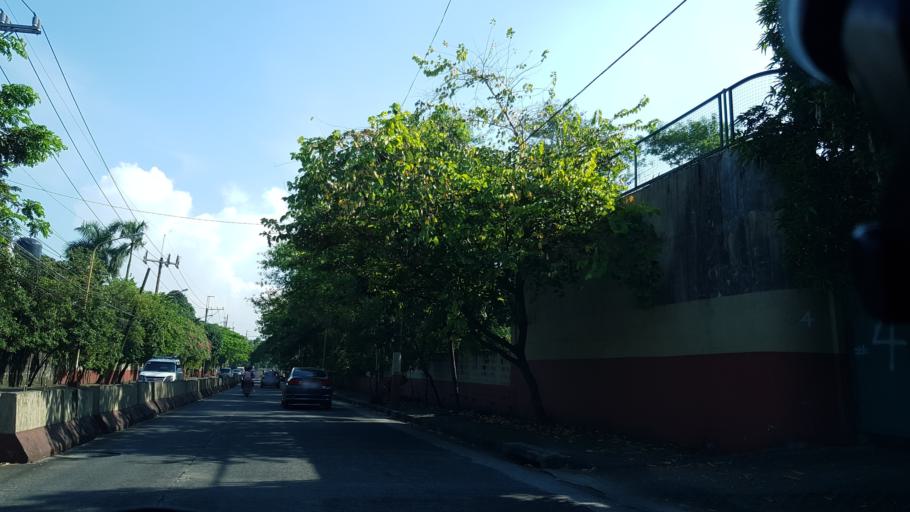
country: PH
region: Metro Manila
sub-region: Pasig
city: Pasig City
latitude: 14.5918
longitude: 121.0724
